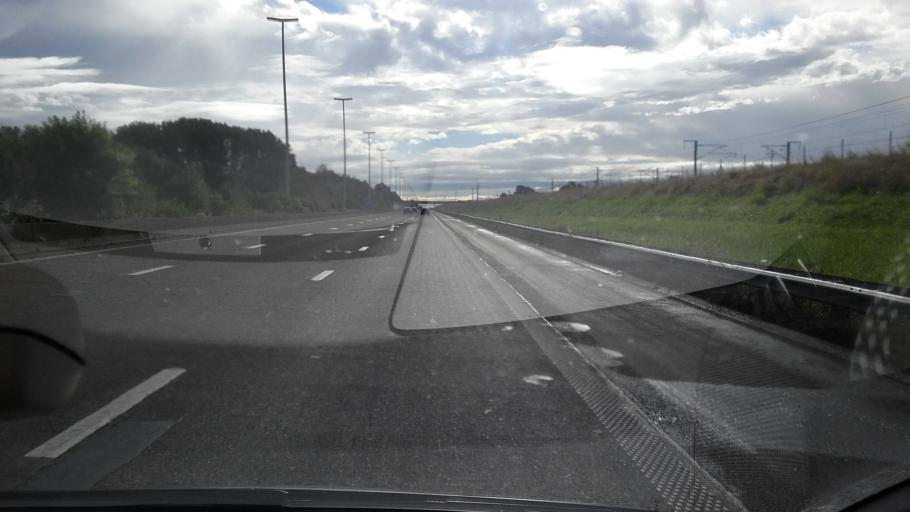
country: BE
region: Wallonia
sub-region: Province de Liege
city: Hannut
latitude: 50.7103
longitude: 5.0933
